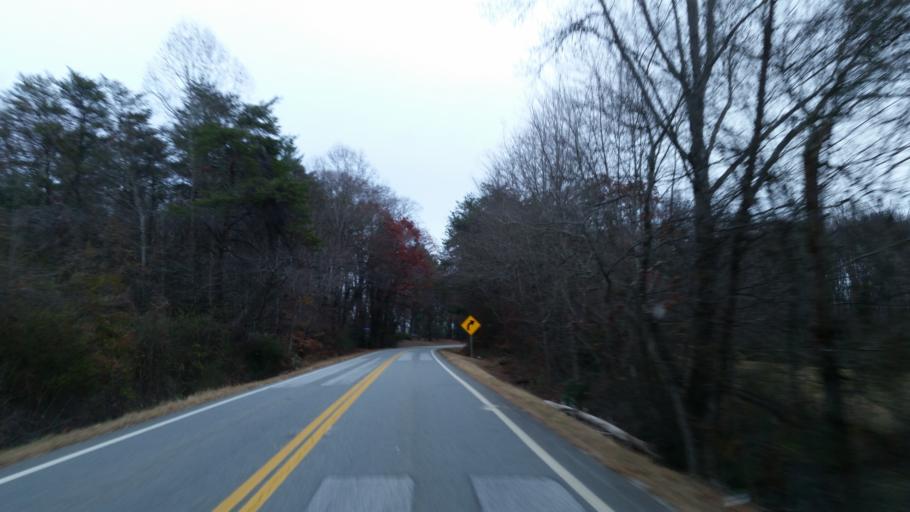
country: US
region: Georgia
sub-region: Dawson County
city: Dawsonville
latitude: 34.4953
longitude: -84.1914
